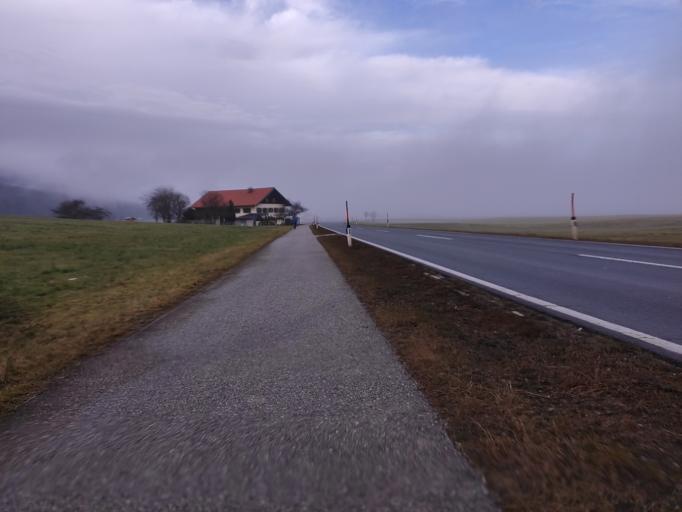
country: AT
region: Upper Austria
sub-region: Politischer Bezirk Vocklabruck
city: Oberhofen am Irrsee
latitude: 47.9629
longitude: 13.2969
